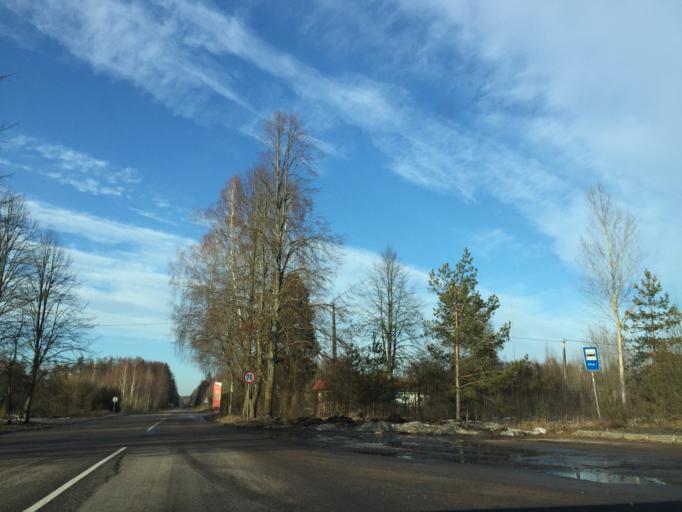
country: LV
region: Kekava
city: Balozi
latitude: 56.7362
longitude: 24.1092
